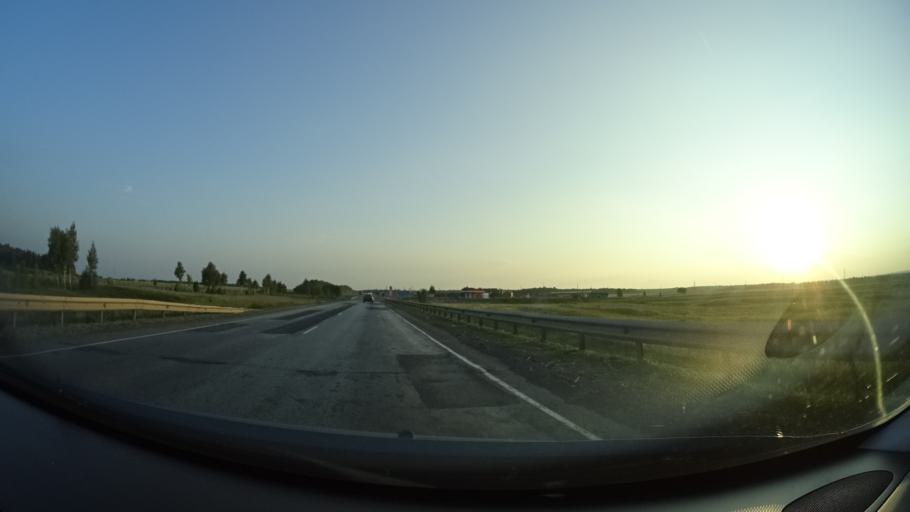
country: RU
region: Samara
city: Sernovodsk
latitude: 53.9338
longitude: 51.3366
